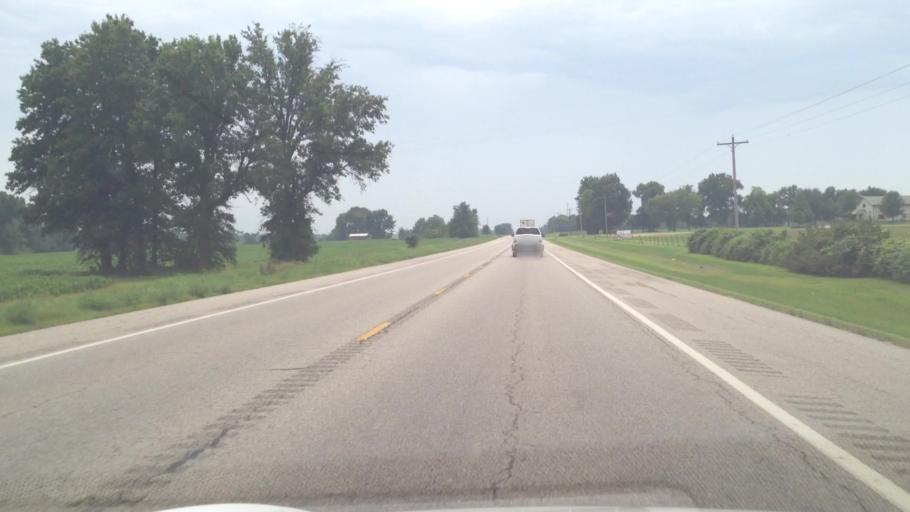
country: US
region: Kansas
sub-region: Cherokee County
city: Galena
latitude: 37.1998
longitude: -94.7047
